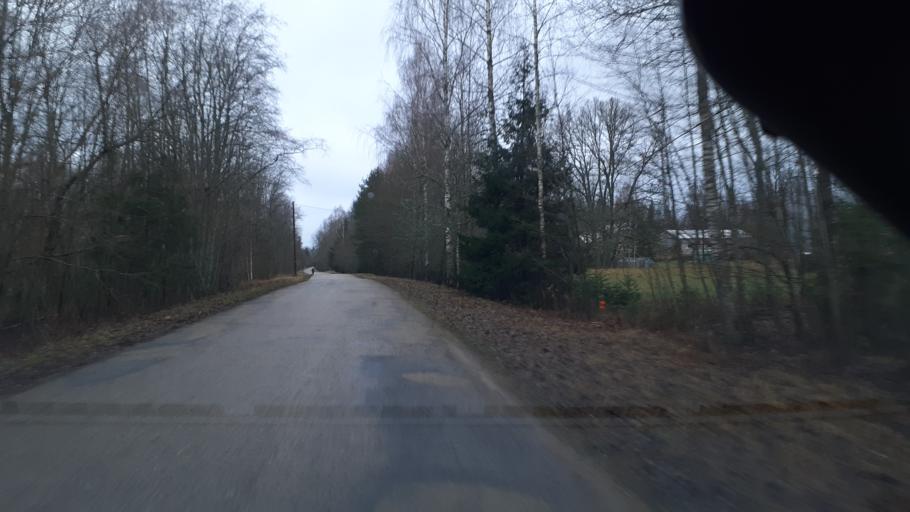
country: LV
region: Kuldigas Rajons
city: Kuldiga
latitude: 56.8811
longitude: 21.8379
